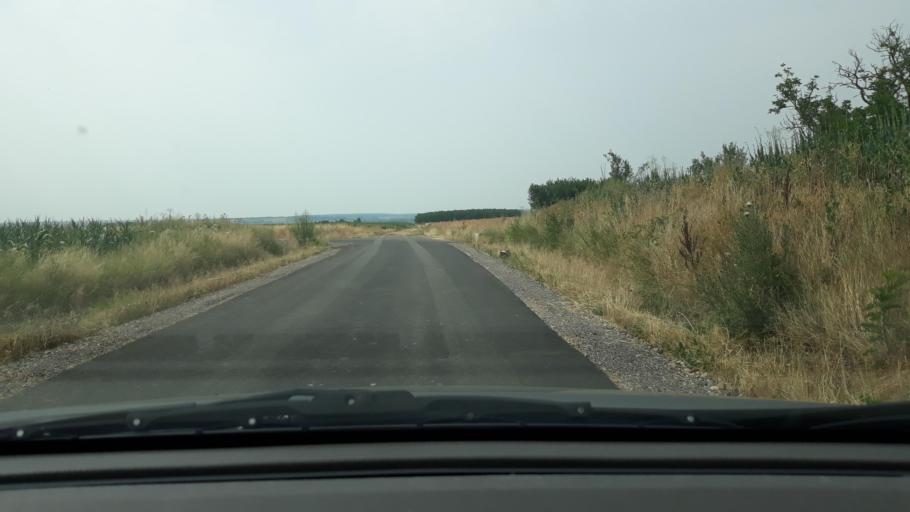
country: RO
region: Bihor
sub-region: Comuna Chislaz
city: Misca
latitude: 47.2786
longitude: 22.2792
